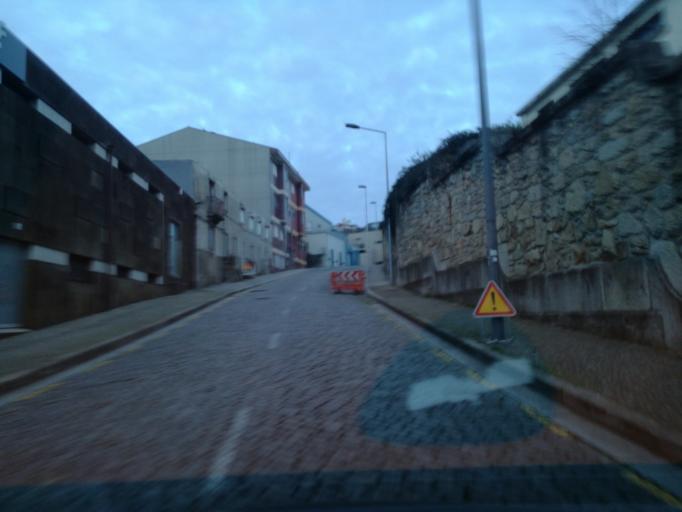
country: PT
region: Porto
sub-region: Vila Nova de Gaia
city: Canidelo
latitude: 41.1489
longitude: -8.6530
